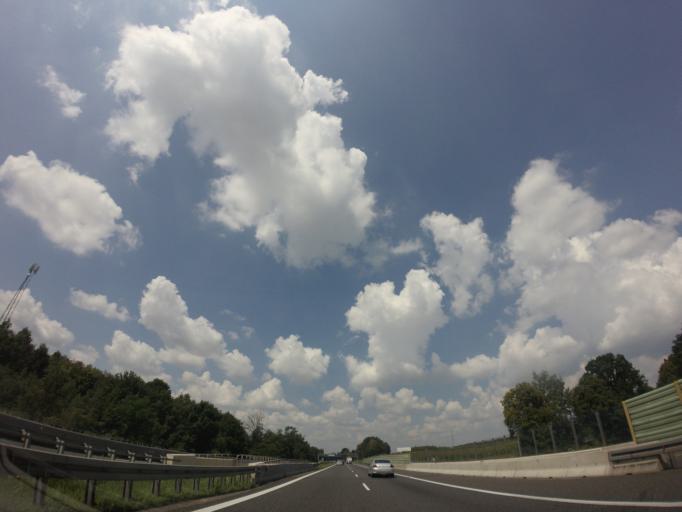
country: PL
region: Opole Voivodeship
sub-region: Powiat strzelecki
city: Ujazd
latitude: 50.4359
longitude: 18.3657
